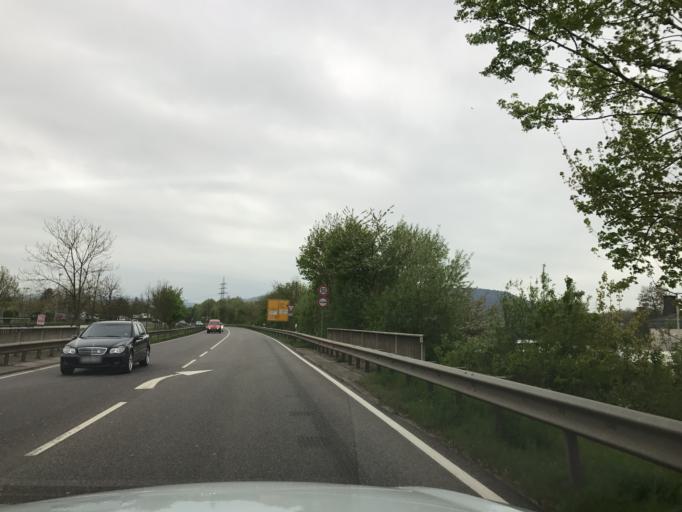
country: DE
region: Rheinland-Pfalz
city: Konz
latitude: 49.7070
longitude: 6.5790
